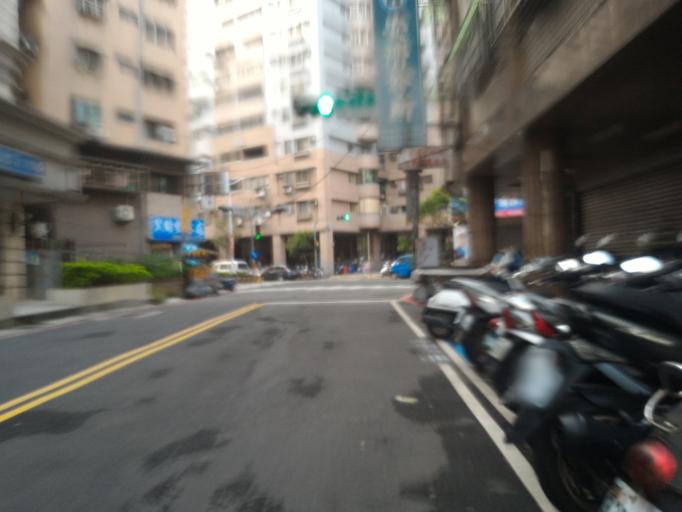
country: TW
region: Taipei
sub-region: Taipei
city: Banqiao
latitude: 24.9802
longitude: 121.4155
